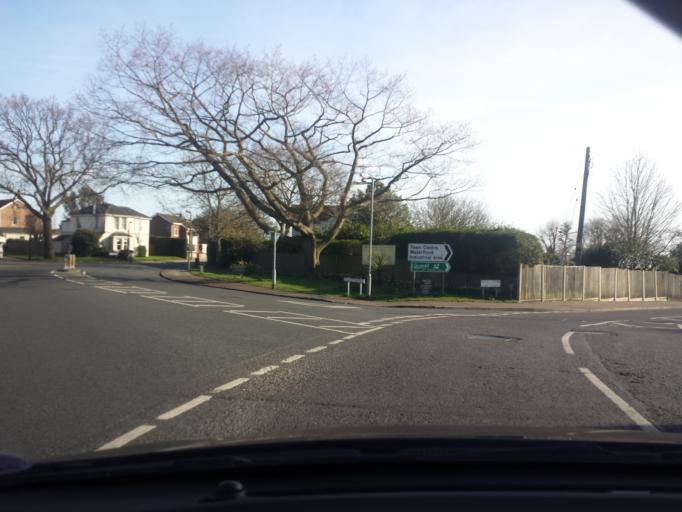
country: GB
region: England
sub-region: Essex
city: Brightlingsea
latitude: 51.8148
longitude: 1.0227
